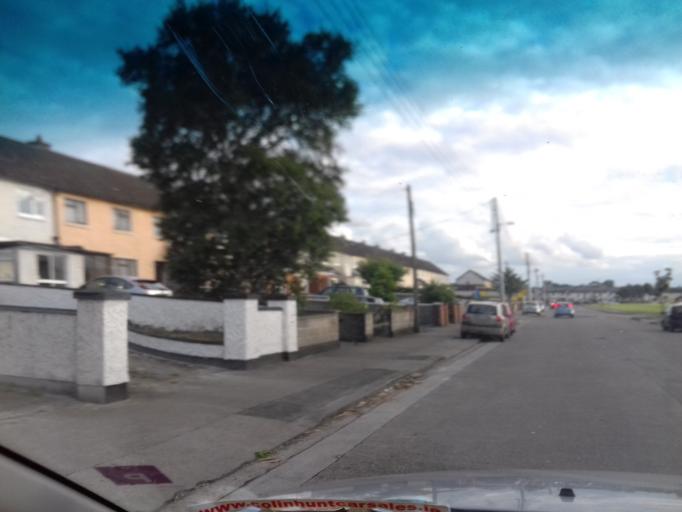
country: IE
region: Leinster
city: Artane
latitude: 53.3957
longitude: -6.2249
